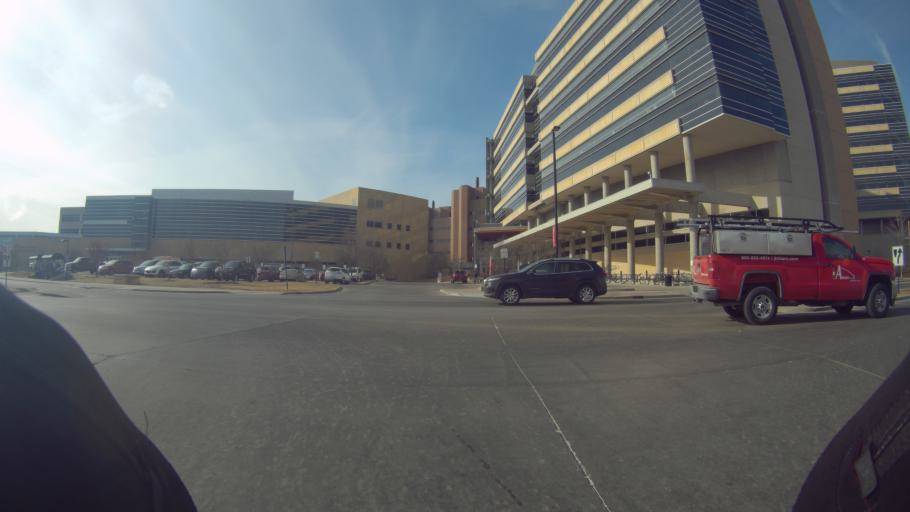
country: US
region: Wisconsin
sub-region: Dane County
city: Shorewood Hills
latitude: 43.0787
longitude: -89.4305
